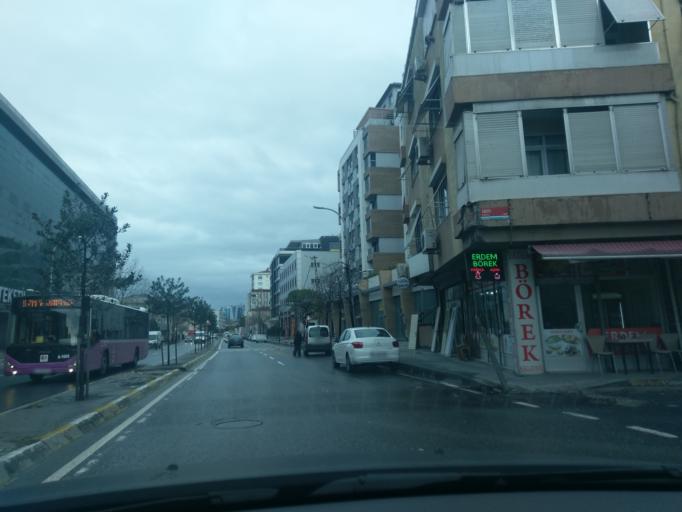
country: TR
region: Istanbul
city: Mahmutbey
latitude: 41.0496
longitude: 28.8303
